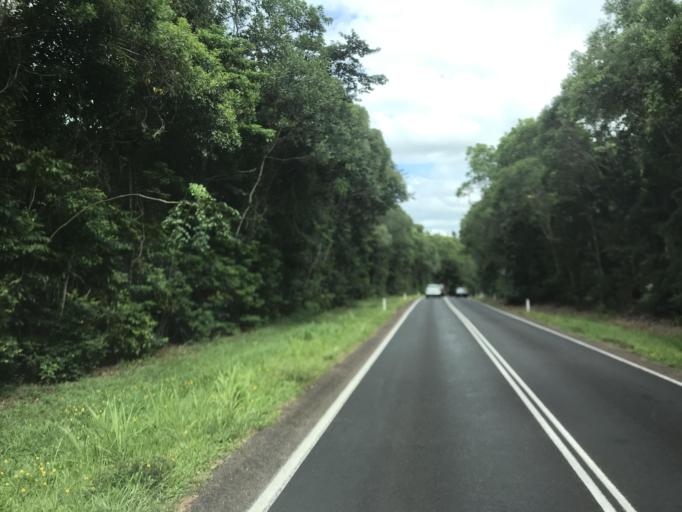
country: AU
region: Queensland
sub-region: Cassowary Coast
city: Innisfail
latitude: -17.8666
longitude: 146.0675
